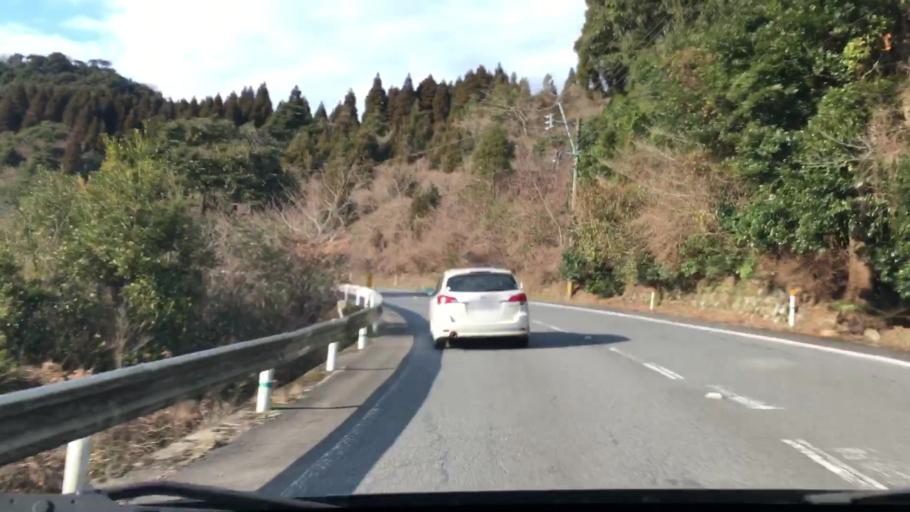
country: JP
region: Miyazaki
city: Miyazaki-shi
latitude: 31.7789
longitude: 131.3301
